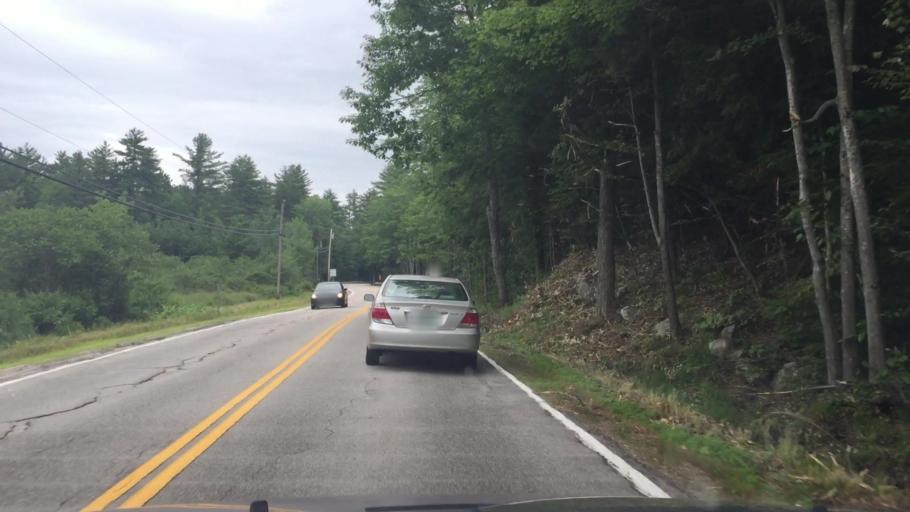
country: US
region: New Hampshire
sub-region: Carroll County
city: Conway
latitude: 43.9190
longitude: -71.0738
